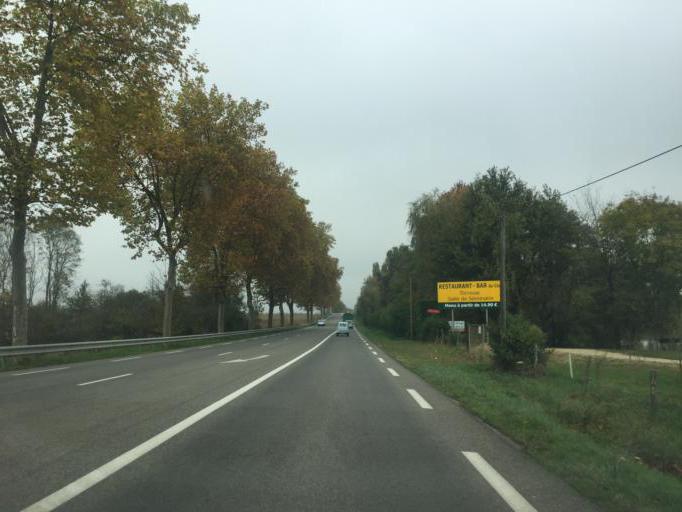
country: FR
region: Rhone-Alpes
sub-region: Departement de l'Ain
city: Villars-les-Dombes
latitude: 45.9734
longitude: 5.0101
